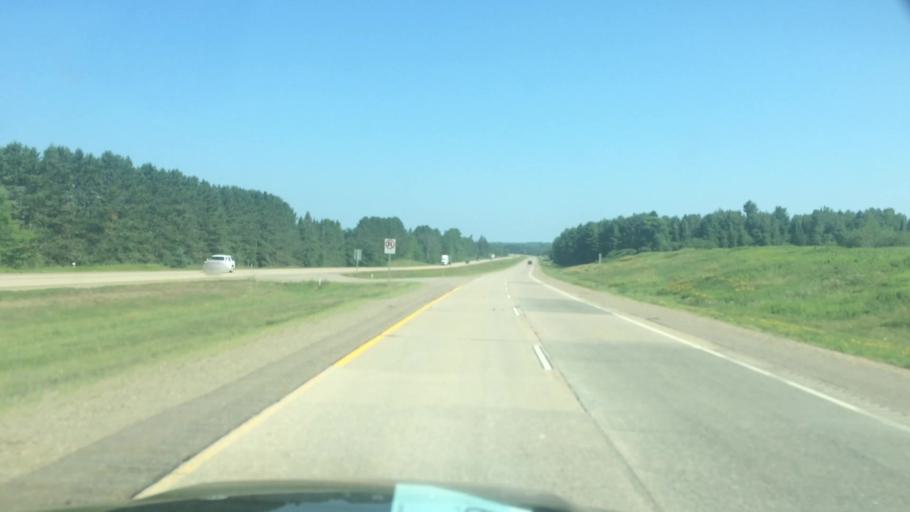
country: US
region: Wisconsin
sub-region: Lincoln County
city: Tomahawk
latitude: 45.3581
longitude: -89.6667
